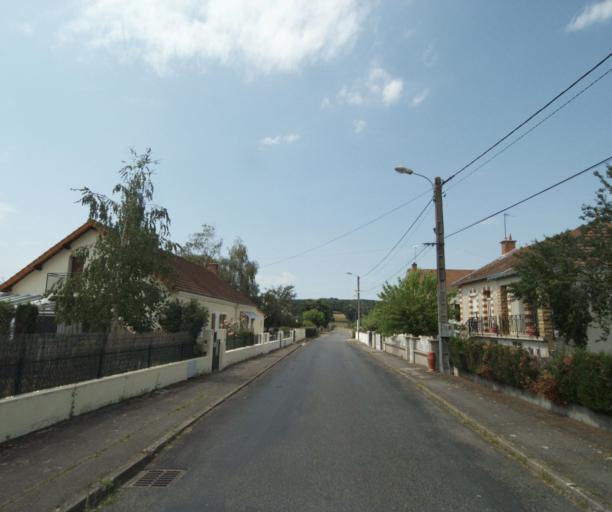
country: FR
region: Bourgogne
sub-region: Departement de Saone-et-Loire
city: Gueugnon
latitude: 46.5994
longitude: 4.0474
